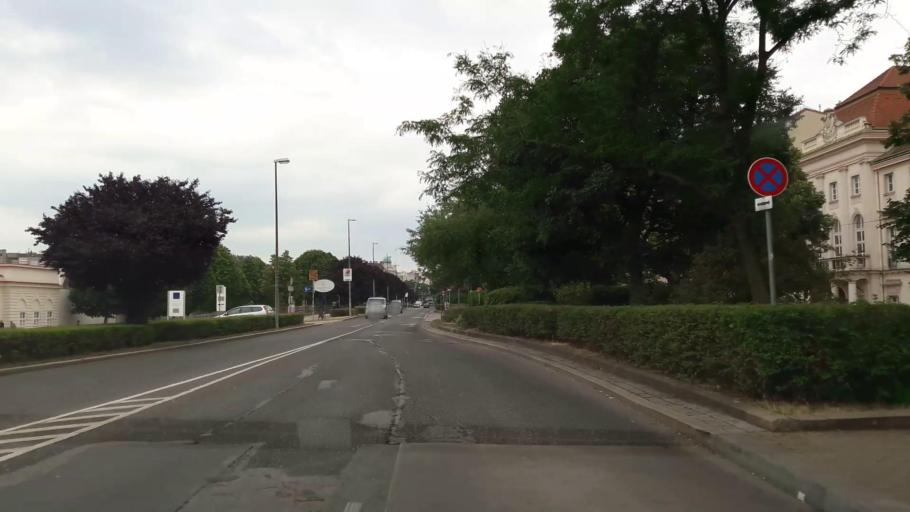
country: AT
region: Vienna
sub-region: Wien Stadt
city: Vienna
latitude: 48.2224
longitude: 16.3760
